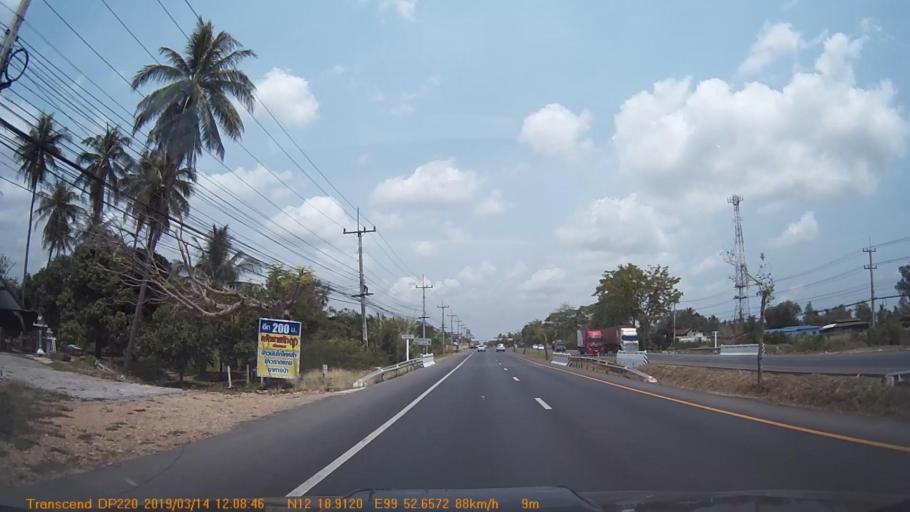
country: TH
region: Prachuap Khiri Khan
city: Sam Roi Yot
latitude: 12.3155
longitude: 99.8777
